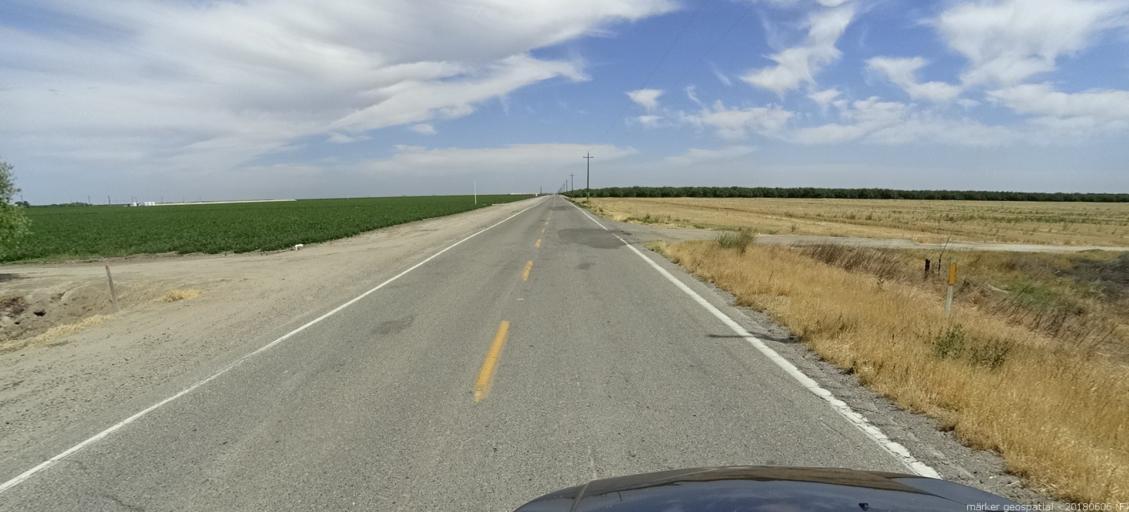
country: US
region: California
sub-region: Fresno County
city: Firebaugh
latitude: 36.8668
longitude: -120.3818
